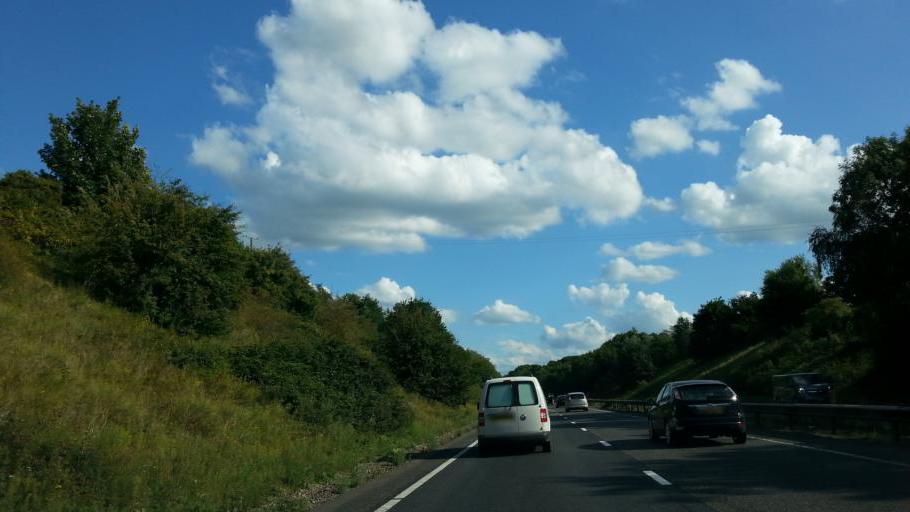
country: GB
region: England
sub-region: Suffolk
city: Needham Market
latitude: 52.1604
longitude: 1.0610
